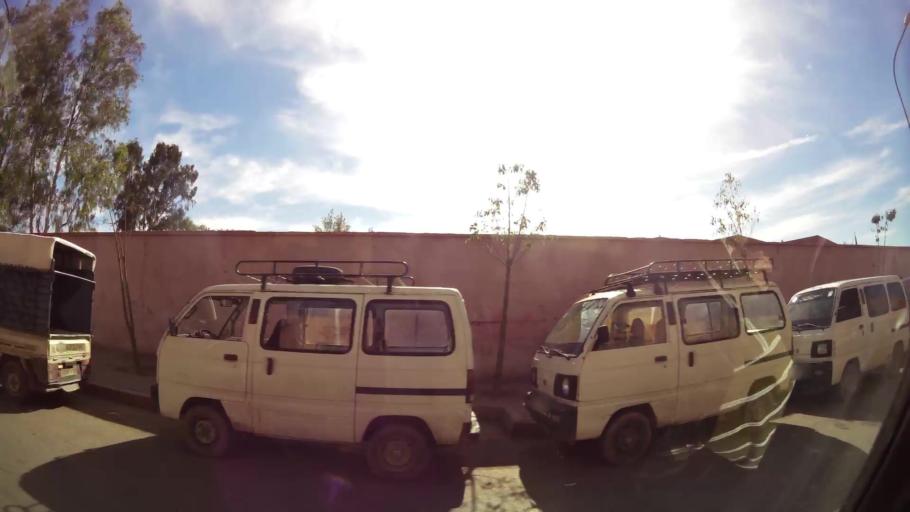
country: MA
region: Marrakech-Tensift-Al Haouz
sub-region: Marrakech
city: Marrakesh
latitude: 31.6071
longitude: -7.9639
